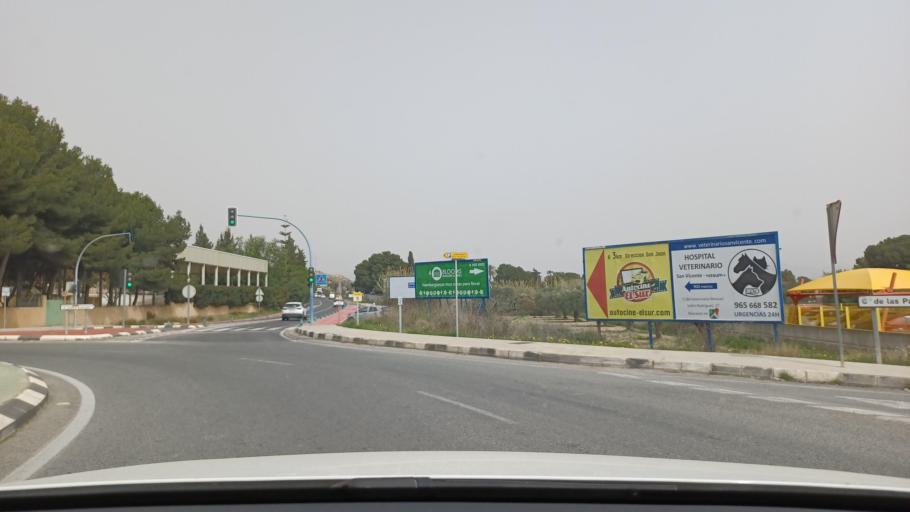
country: ES
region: Valencia
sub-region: Provincia de Alicante
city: San Vicent del Raspeig
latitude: 38.3854
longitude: -0.4882
